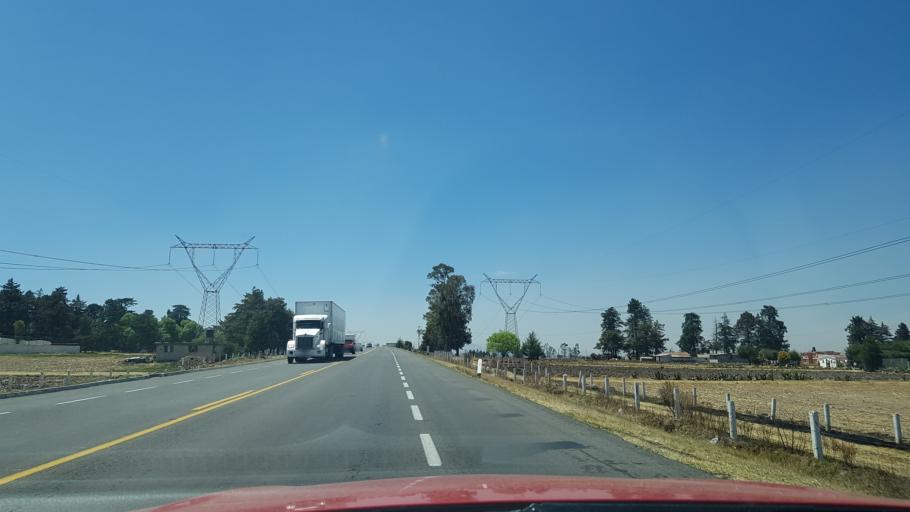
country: MX
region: Mexico
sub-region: Toluca
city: Sebastian Lerdo de Tejada
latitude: 19.3878
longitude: -99.7350
